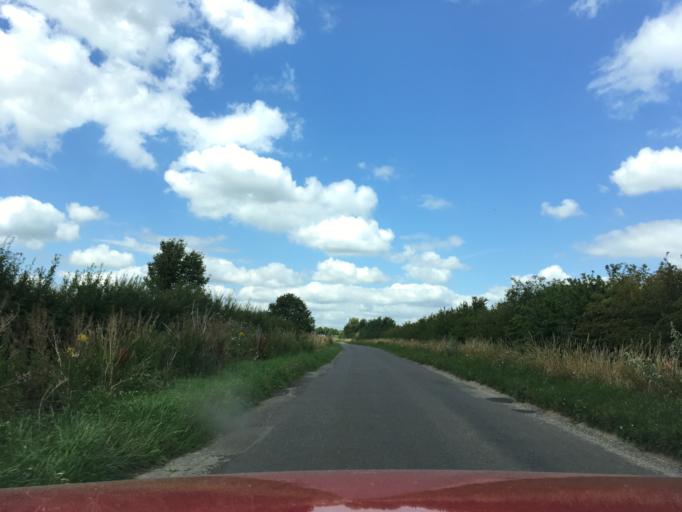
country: GB
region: England
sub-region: Oxfordshire
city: Faringdon
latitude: 51.6225
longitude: -1.6149
